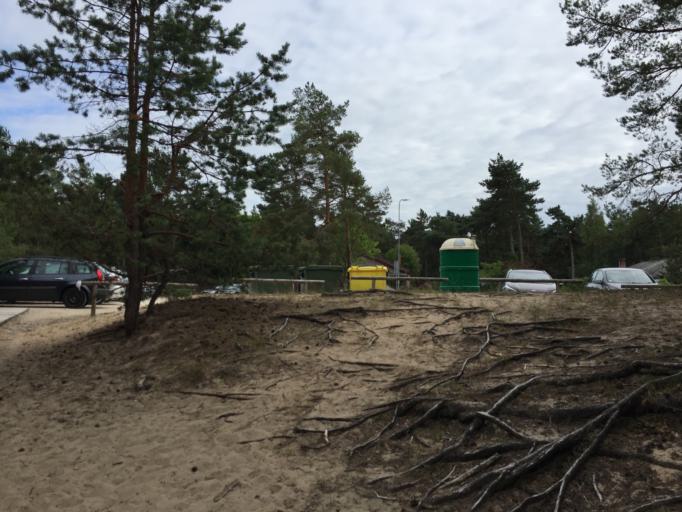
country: LV
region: Carnikava
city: Carnikava
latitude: 57.1365
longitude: 24.2465
